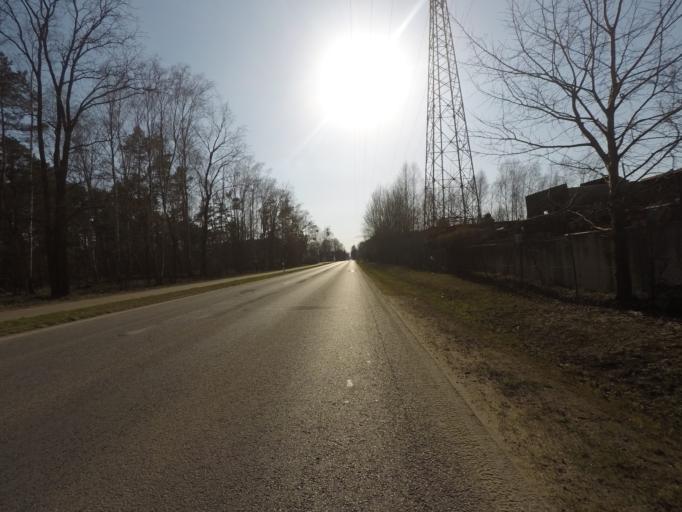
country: DE
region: Brandenburg
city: Eberswalde
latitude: 52.8498
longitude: 13.7547
